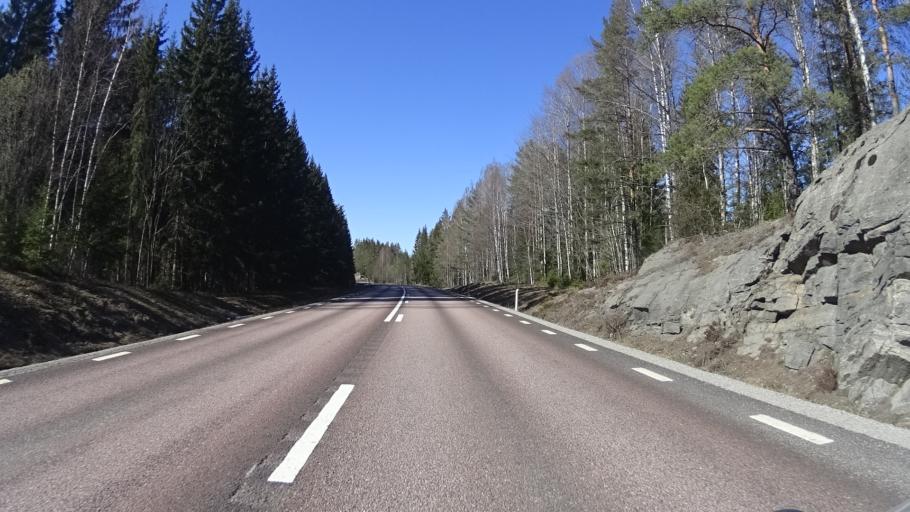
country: SE
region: Vaermland
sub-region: Karlstads Kommun
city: Edsvalla
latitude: 59.6116
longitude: 12.9873
